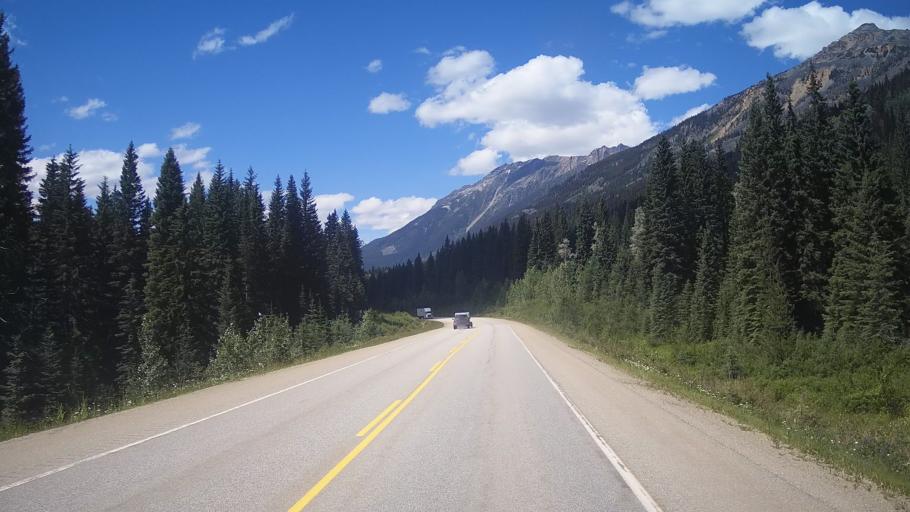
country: CA
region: Alberta
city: Grande Cache
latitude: 52.9992
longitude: -119.0287
